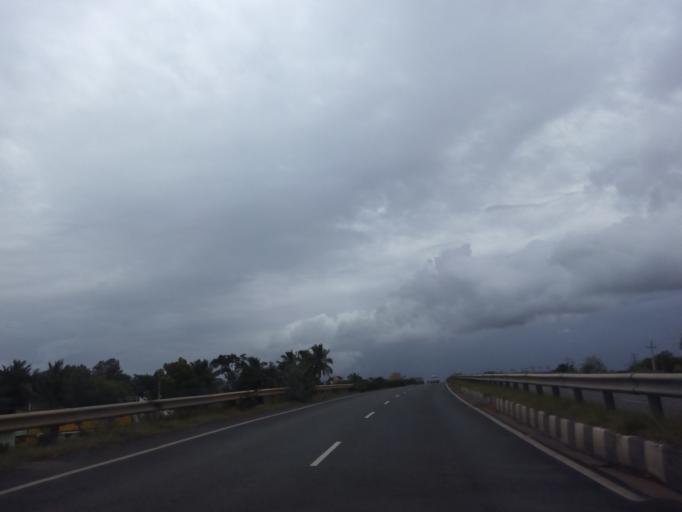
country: IN
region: Karnataka
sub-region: Haveri
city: Ranibennur
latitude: 14.5642
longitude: 75.7156
